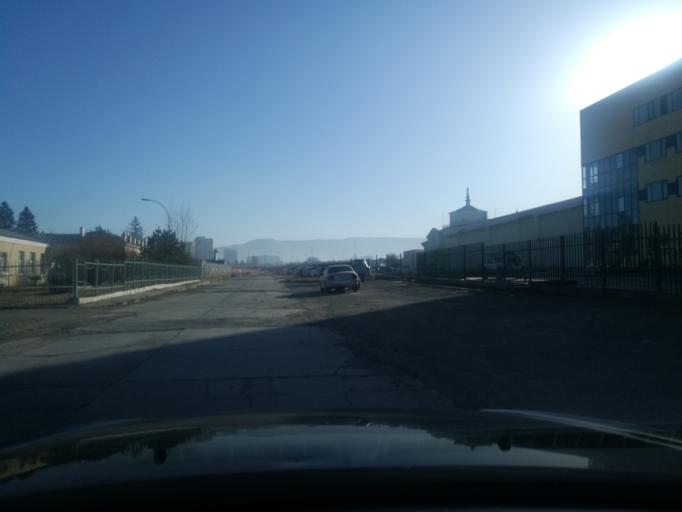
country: MN
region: Ulaanbaatar
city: Ulaanbaatar
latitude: 47.8543
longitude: 106.7585
